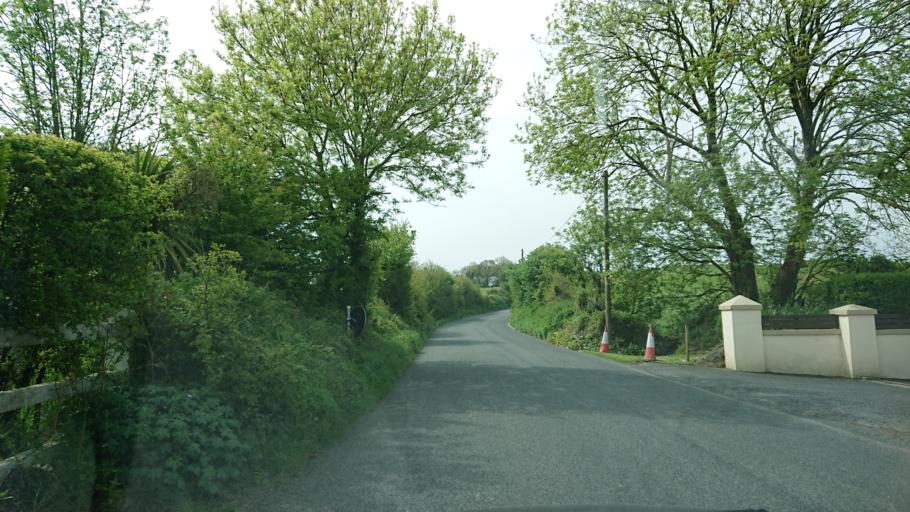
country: IE
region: Munster
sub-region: Waterford
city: Waterford
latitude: 52.2187
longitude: -7.0737
